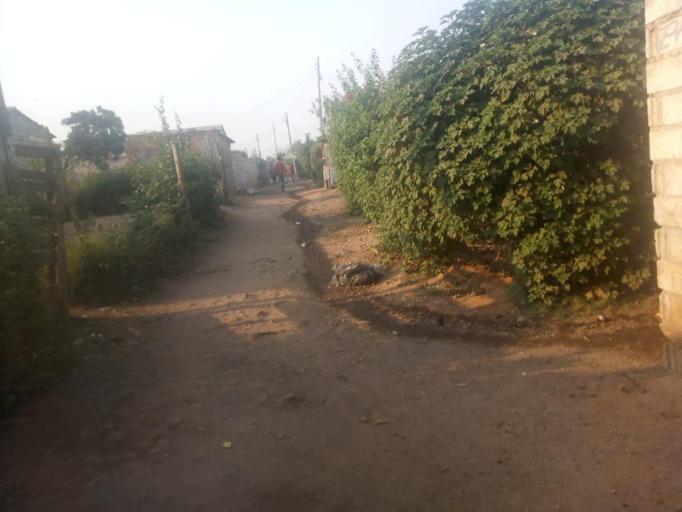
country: ZM
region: Lusaka
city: Lusaka
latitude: -15.4070
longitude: 28.3659
